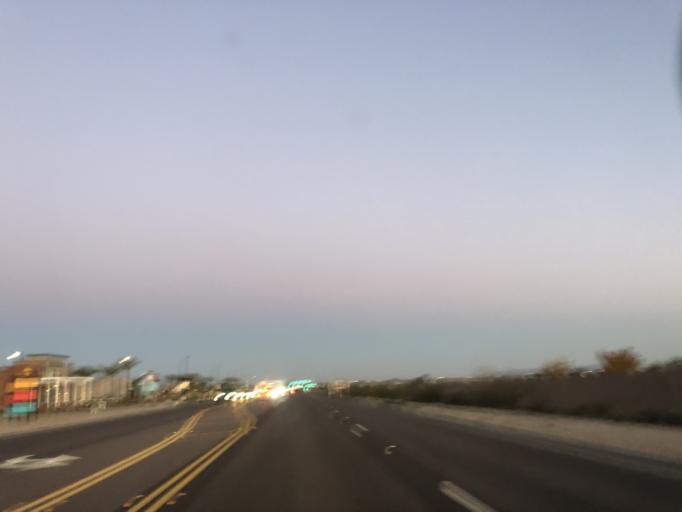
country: US
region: Arizona
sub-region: Maricopa County
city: Citrus Park
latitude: 33.4937
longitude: -112.4845
